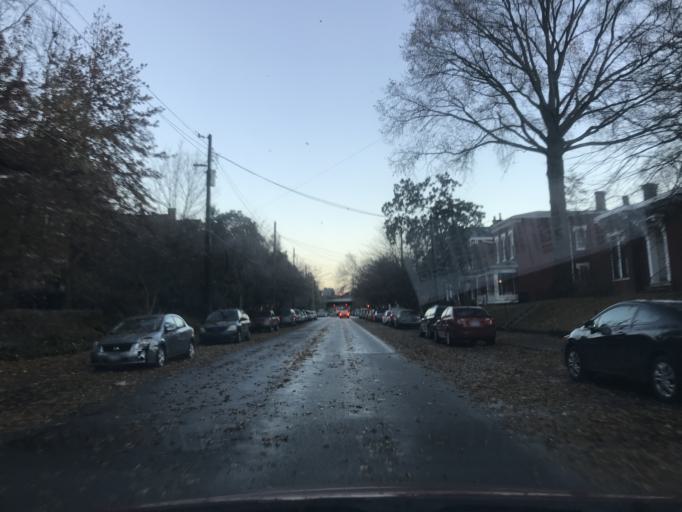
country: US
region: Kentucky
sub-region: Jefferson County
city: Louisville
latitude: 38.2355
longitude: -85.7535
